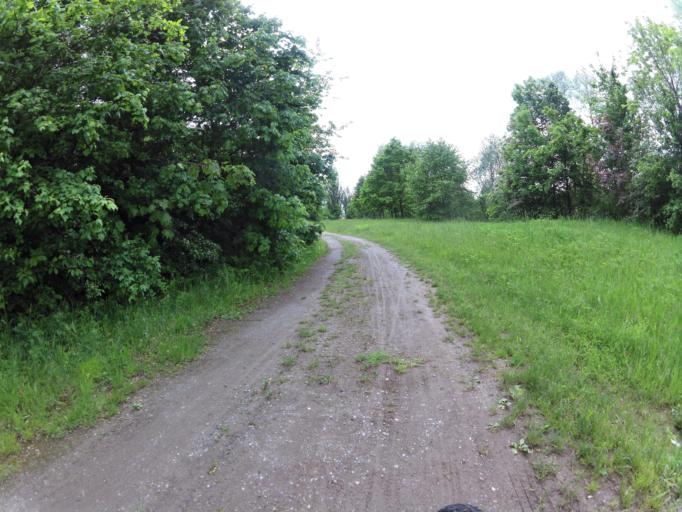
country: DE
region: Bavaria
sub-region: Regierungsbezirk Unterfranken
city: Sommerach
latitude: 49.8231
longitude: 10.2101
